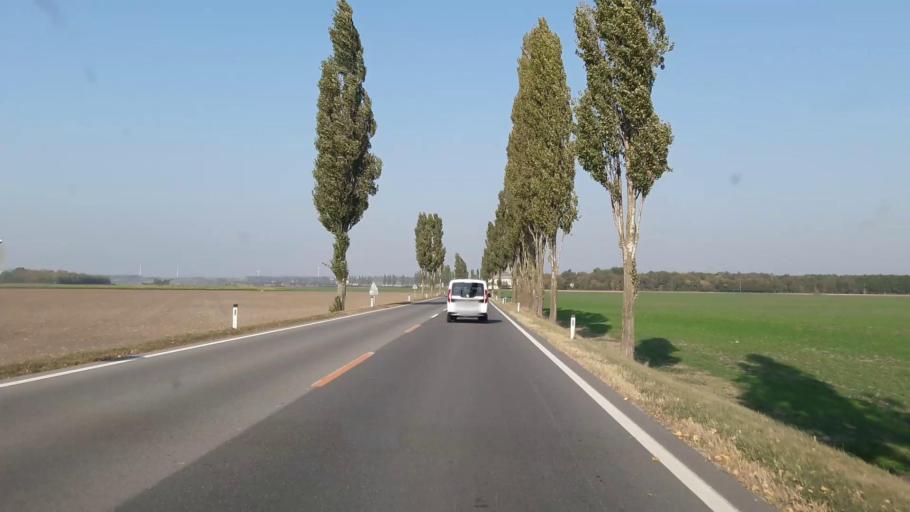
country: AT
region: Lower Austria
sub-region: Politischer Bezirk Ganserndorf
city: Engelhartstetten
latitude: 48.1904
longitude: 16.8969
